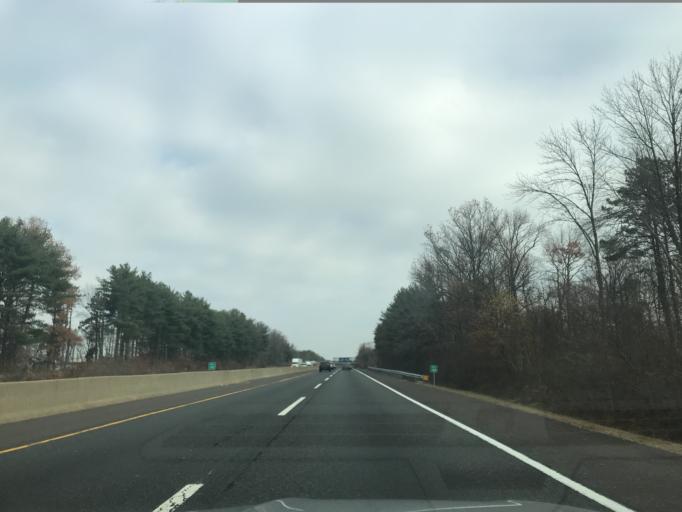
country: US
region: New Jersey
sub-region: Camden County
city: Springdale
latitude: 39.9035
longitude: -74.9836
